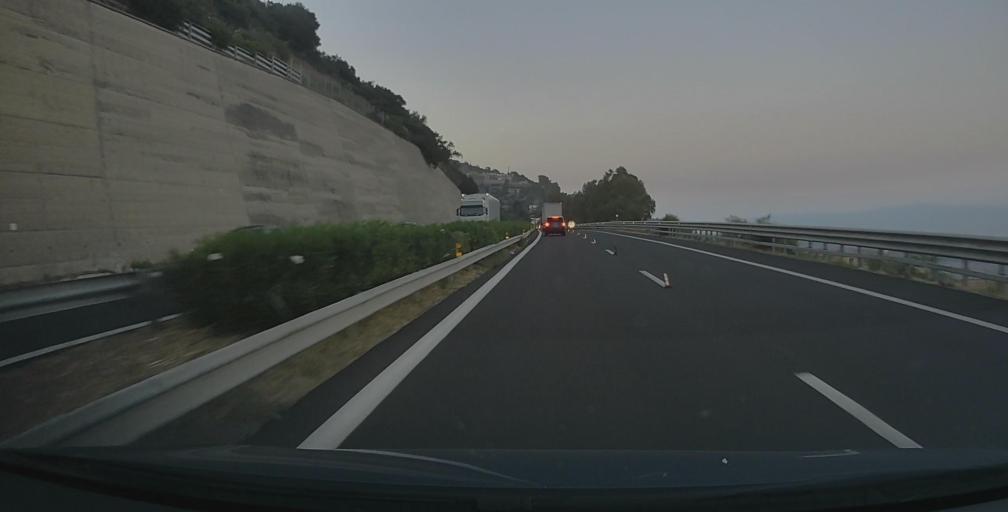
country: IT
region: Sicily
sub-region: Messina
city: Guidomandri Marina
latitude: 38.0351
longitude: 15.4501
